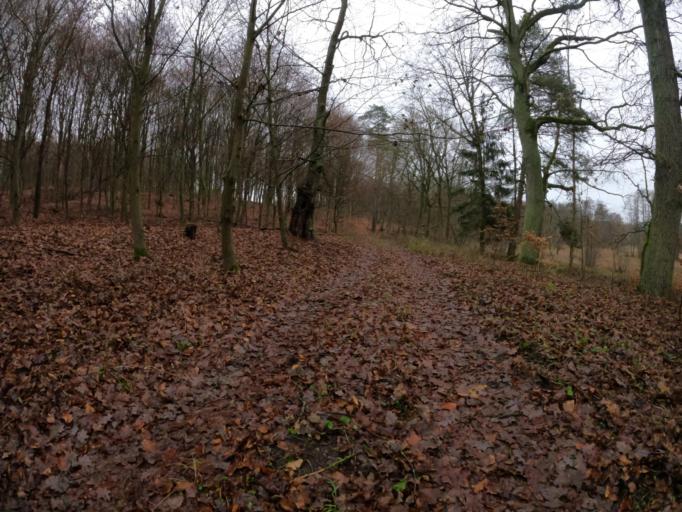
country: PL
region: West Pomeranian Voivodeship
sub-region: Powiat mysliborski
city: Debno
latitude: 52.7534
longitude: 14.7684
